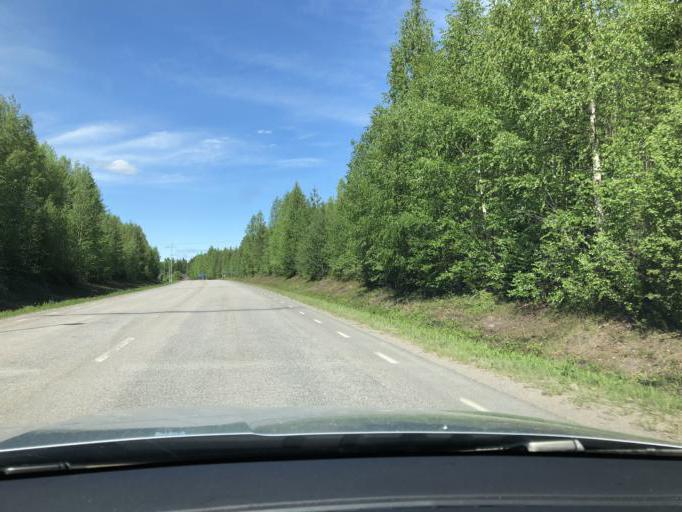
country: SE
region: Norrbotten
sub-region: Pitea Kommun
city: Bergsviken
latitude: 65.3817
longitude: 21.3378
